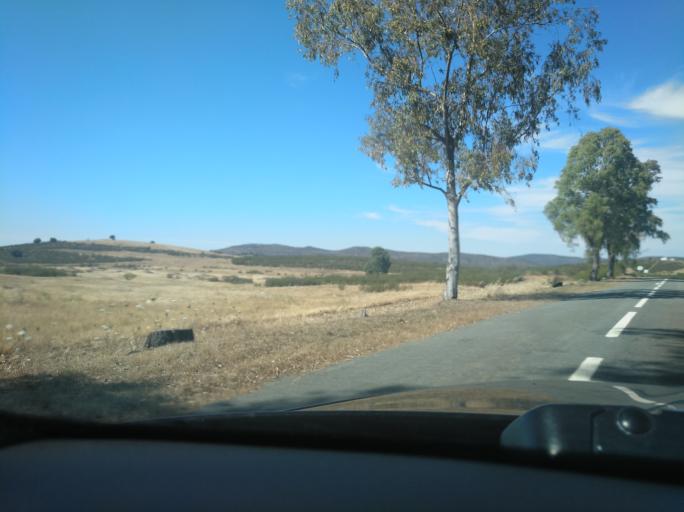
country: PT
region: Beja
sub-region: Mertola
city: Mertola
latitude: 37.6093
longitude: -7.7980
